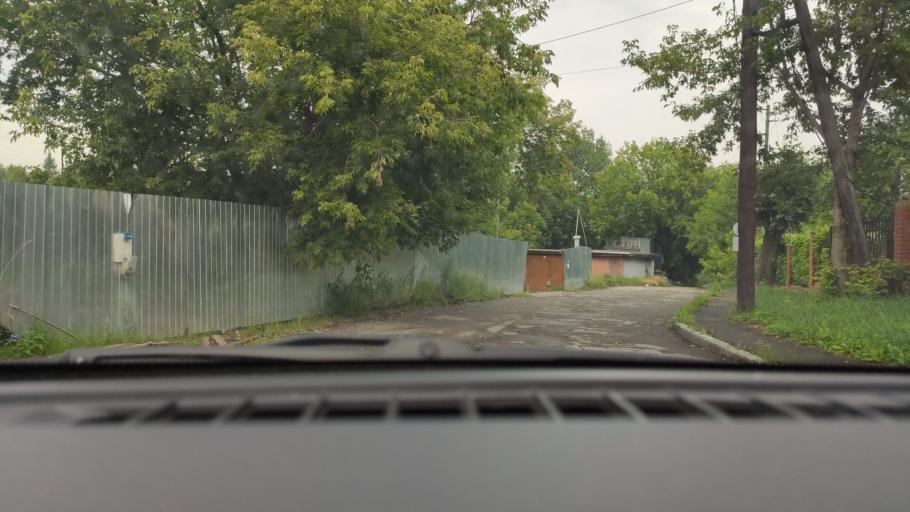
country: RU
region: Perm
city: Perm
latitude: 58.0186
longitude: 56.2577
